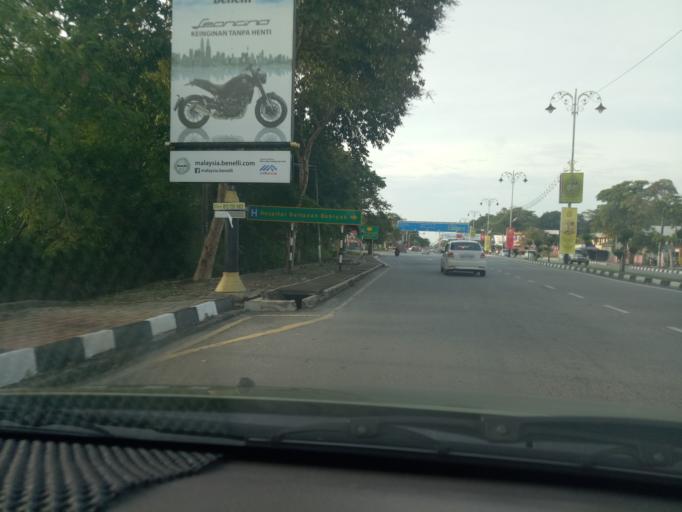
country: MY
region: Kedah
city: Alor Setar
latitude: 6.1420
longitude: 100.3704
